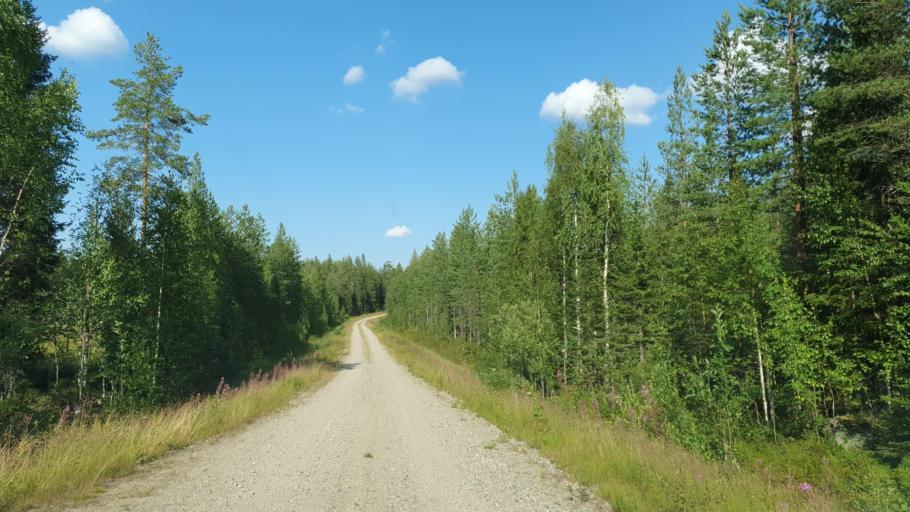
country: FI
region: Kainuu
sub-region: Kehys-Kainuu
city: Kuhmo
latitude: 63.9626
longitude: 29.5380
